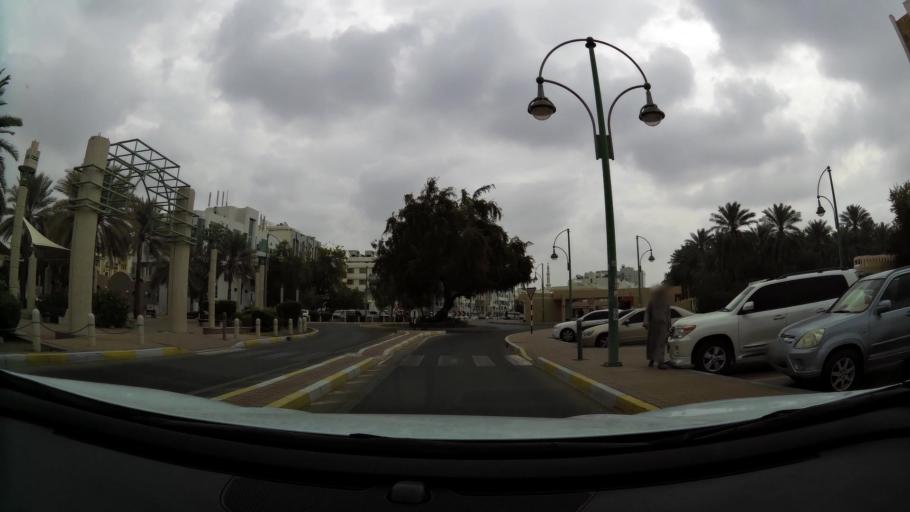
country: AE
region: Abu Dhabi
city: Al Ain
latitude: 24.2215
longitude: 55.7667
